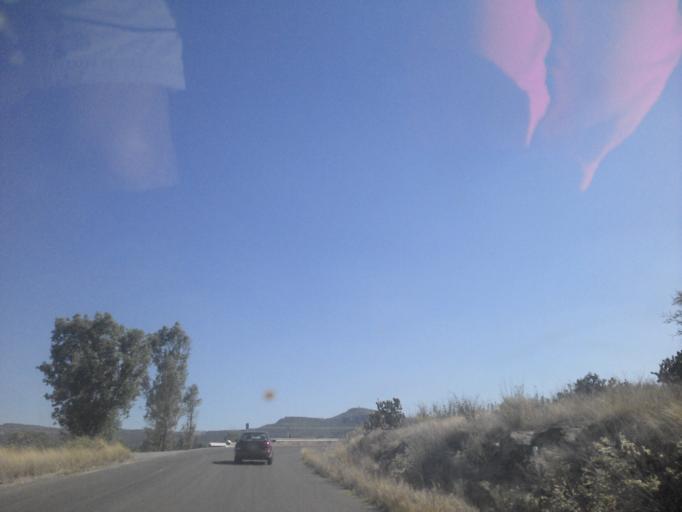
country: MX
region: Jalisco
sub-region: Arandas
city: Santiaguito (Santiaguito de Velazquez)
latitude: 20.8286
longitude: -102.1313
